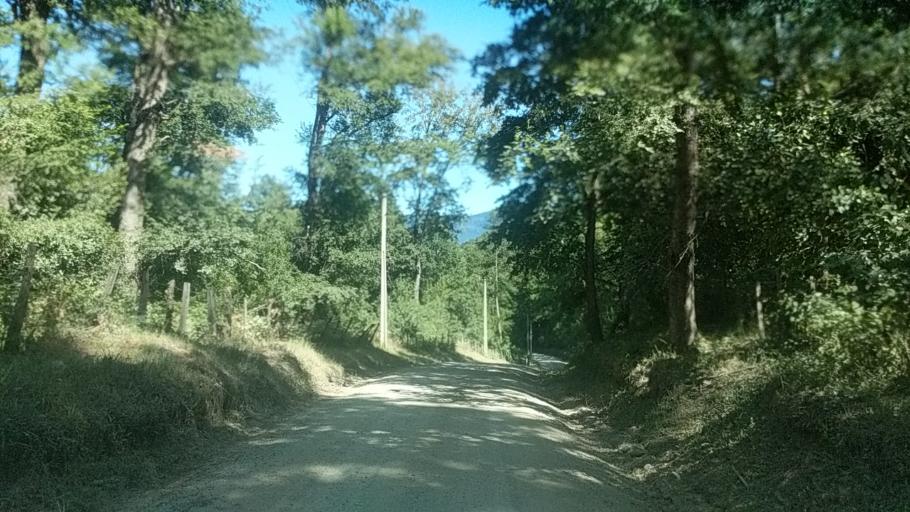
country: CL
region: Araucania
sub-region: Provincia de Cautin
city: Pucon
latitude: -39.0652
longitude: -71.7384
